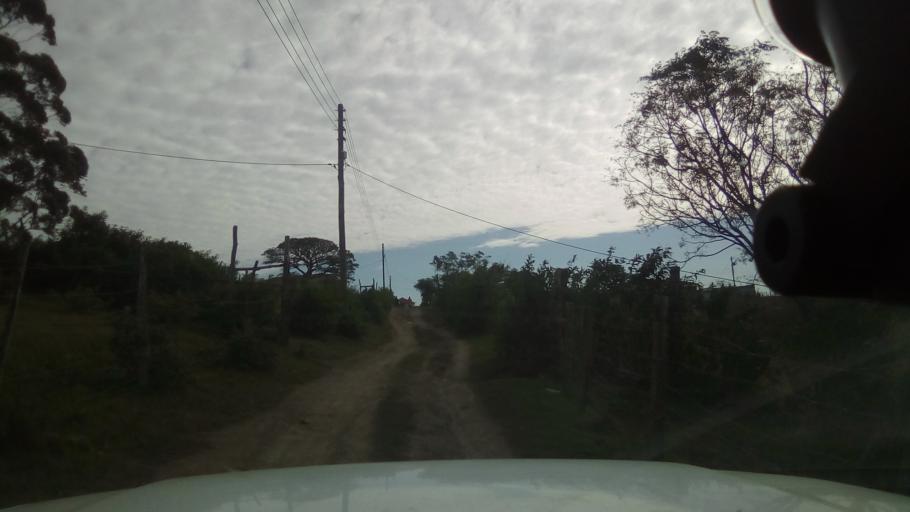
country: ZA
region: Eastern Cape
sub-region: Buffalo City Metropolitan Municipality
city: East London
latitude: -32.7953
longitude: 27.9570
